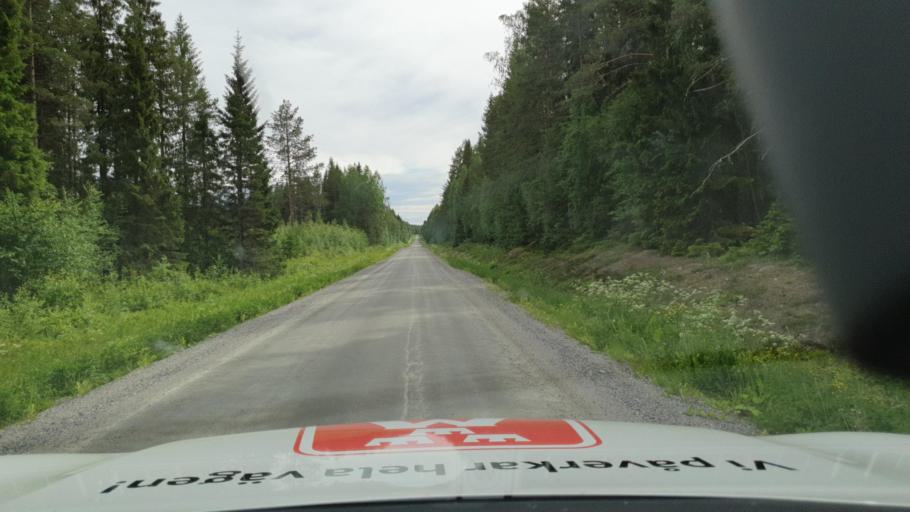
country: SE
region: Vaesterbotten
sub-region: Skelleftea Kommun
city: Burea
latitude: 64.4381
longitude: 21.0165
